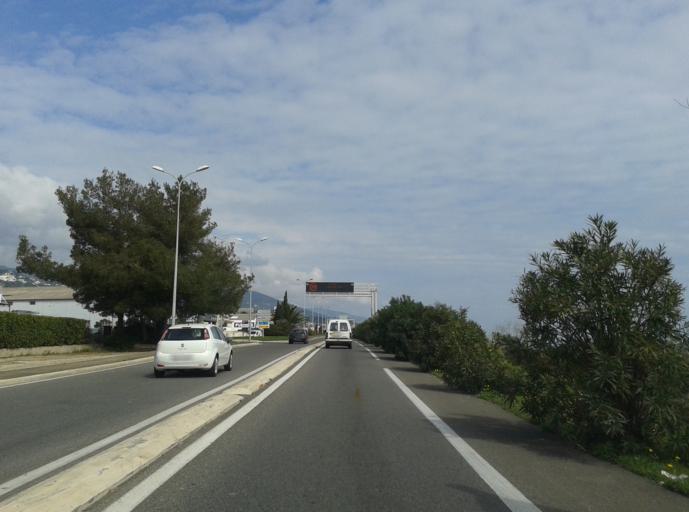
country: FR
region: Corsica
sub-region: Departement de la Haute-Corse
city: Furiani
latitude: 42.6709
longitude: 9.4435
